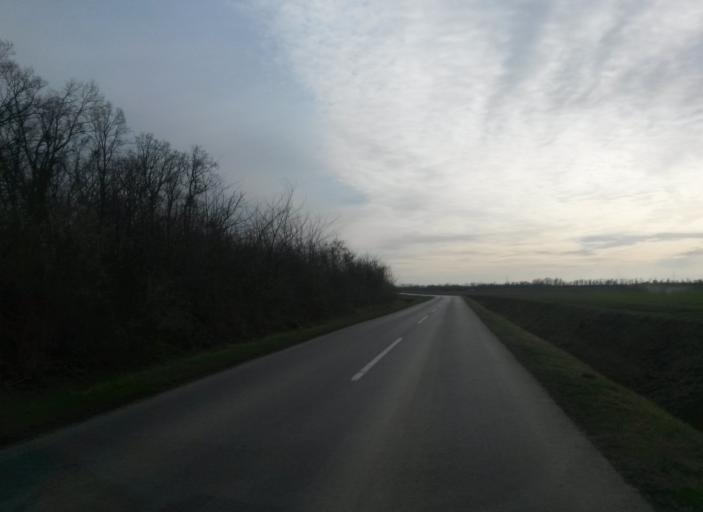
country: HR
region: Osjecko-Baranjska
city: Ovcara
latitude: 45.5089
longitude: 18.5954
